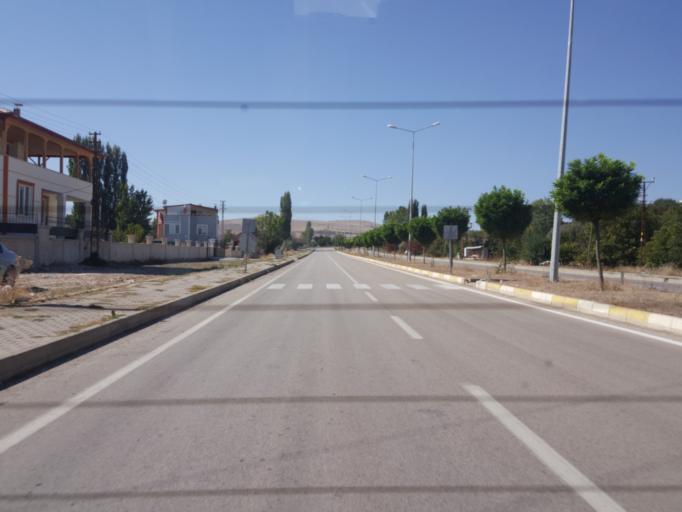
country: TR
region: Tokat
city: Zile
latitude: 40.2838
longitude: 35.8602
